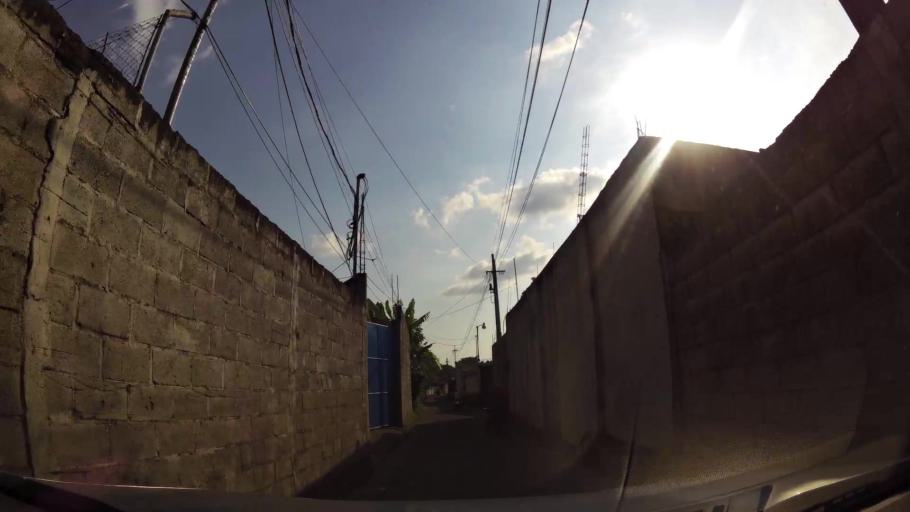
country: GT
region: Retalhuleu
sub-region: Municipio de Retalhuleu
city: Retalhuleu
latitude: 14.5313
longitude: -91.6770
